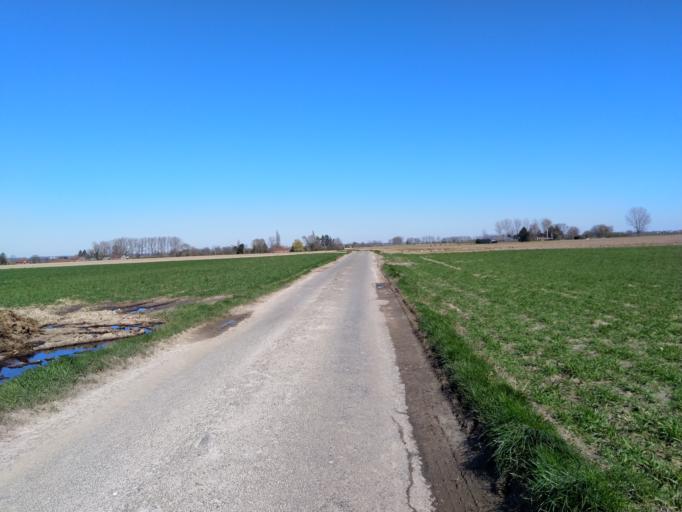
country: BE
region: Wallonia
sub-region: Province du Hainaut
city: Jurbise
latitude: 50.5490
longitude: 3.9224
